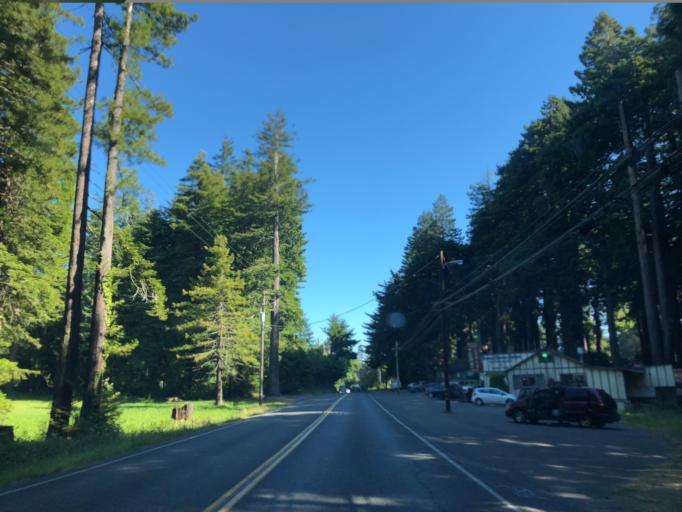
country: US
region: California
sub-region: Humboldt County
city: Westhaven-Moonstone
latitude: 41.0687
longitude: -124.1431
